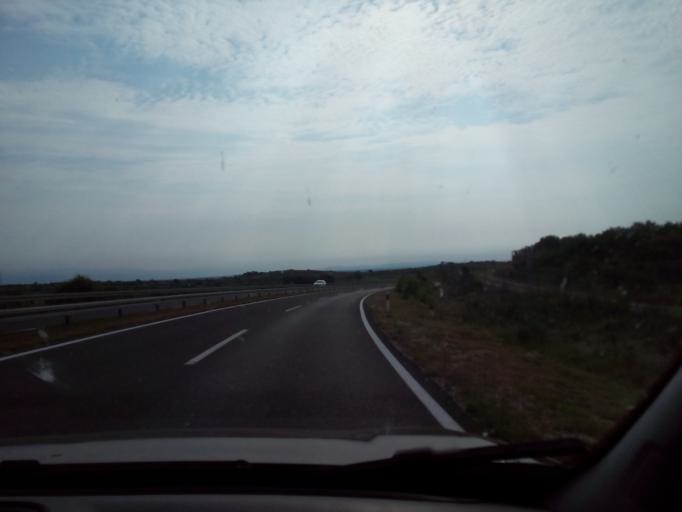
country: HR
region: Zadarska
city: Bibinje
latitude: 44.0981
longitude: 15.2878
